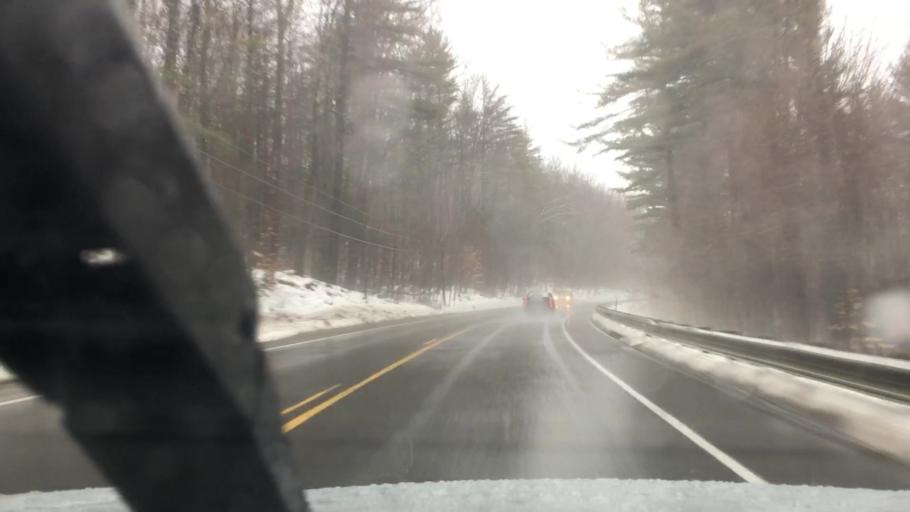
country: US
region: Massachusetts
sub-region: Franklin County
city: Wendell
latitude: 42.5109
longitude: -72.3287
